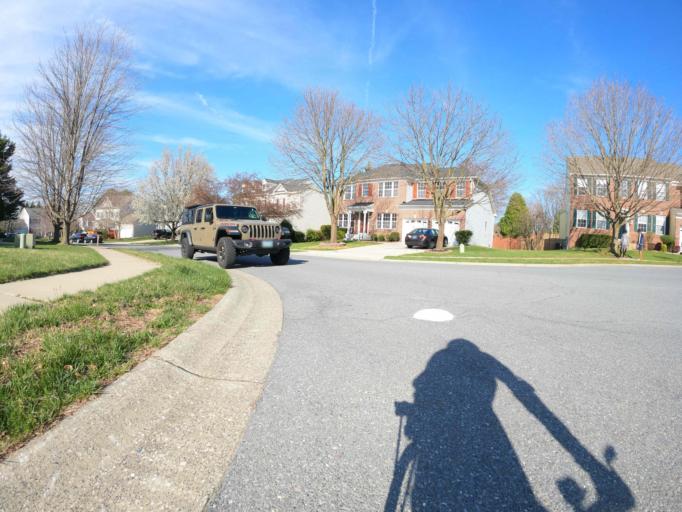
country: US
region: Maryland
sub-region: Howard County
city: Ellicott City
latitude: 39.3004
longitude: -76.8116
